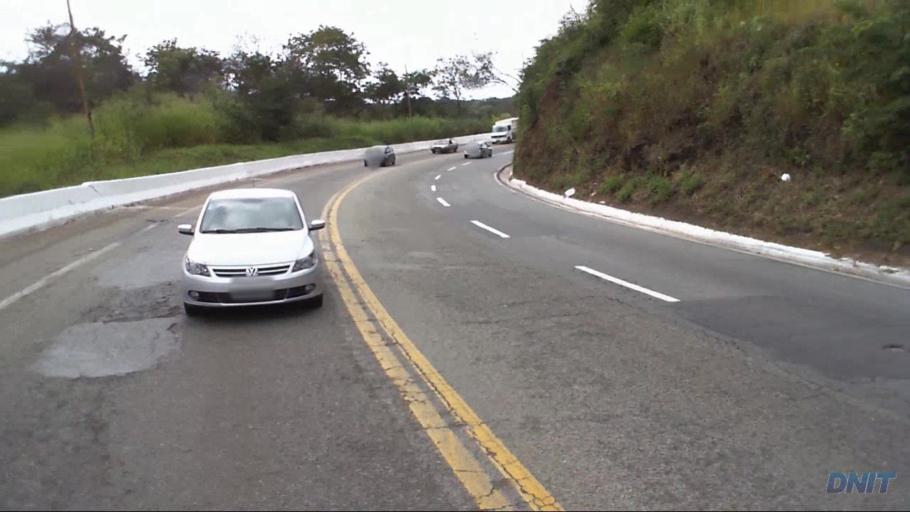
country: BR
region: Minas Gerais
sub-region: Caete
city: Caete
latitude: -19.7865
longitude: -43.7346
